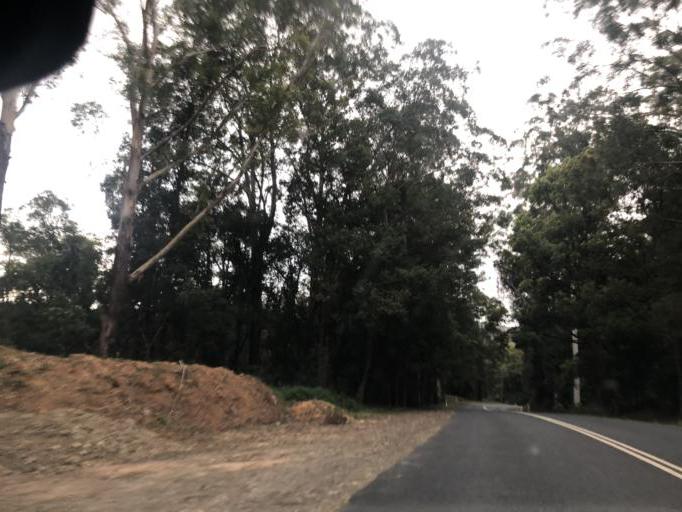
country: AU
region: New South Wales
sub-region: Coffs Harbour
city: Boambee
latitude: -30.2626
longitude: 153.0205
